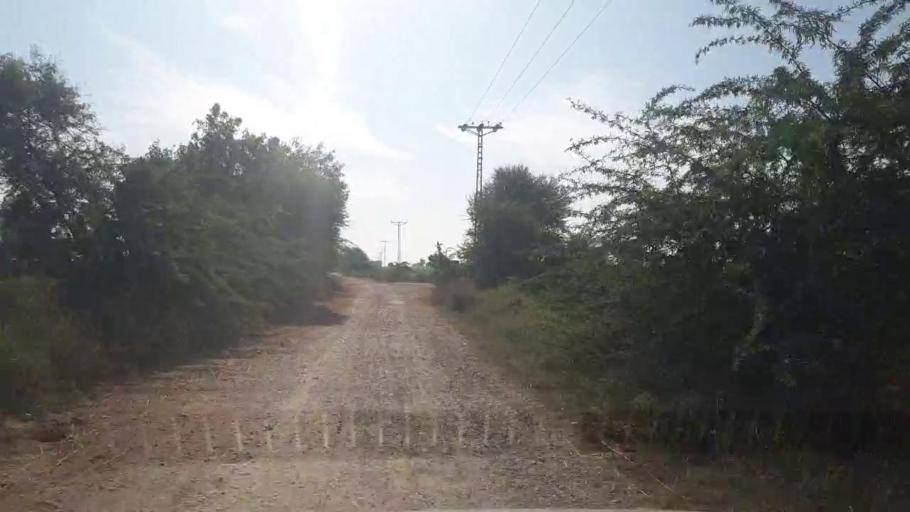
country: PK
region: Sindh
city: Talhar
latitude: 24.9397
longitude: 68.7969
